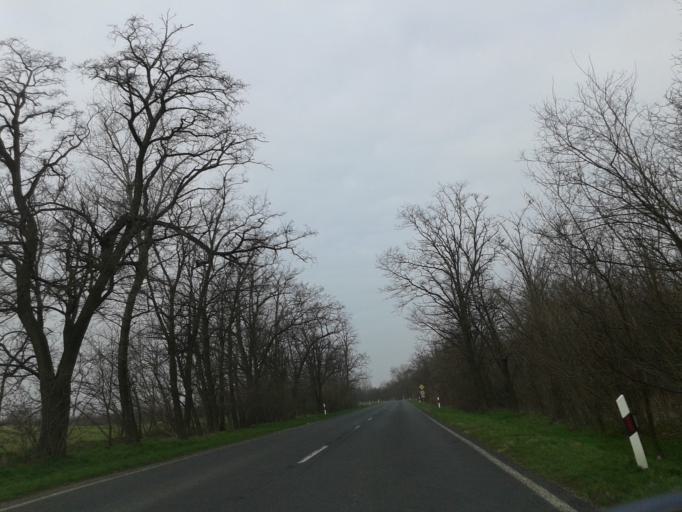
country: HU
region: Komarom-Esztergom
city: Acs
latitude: 47.7377
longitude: 17.9662
